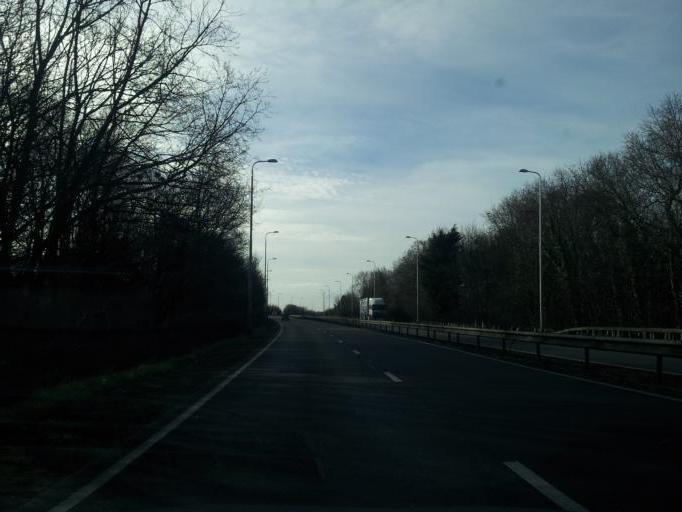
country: GB
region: England
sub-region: Central Bedfordshire
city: Tempsford
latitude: 52.1658
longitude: -0.3011
